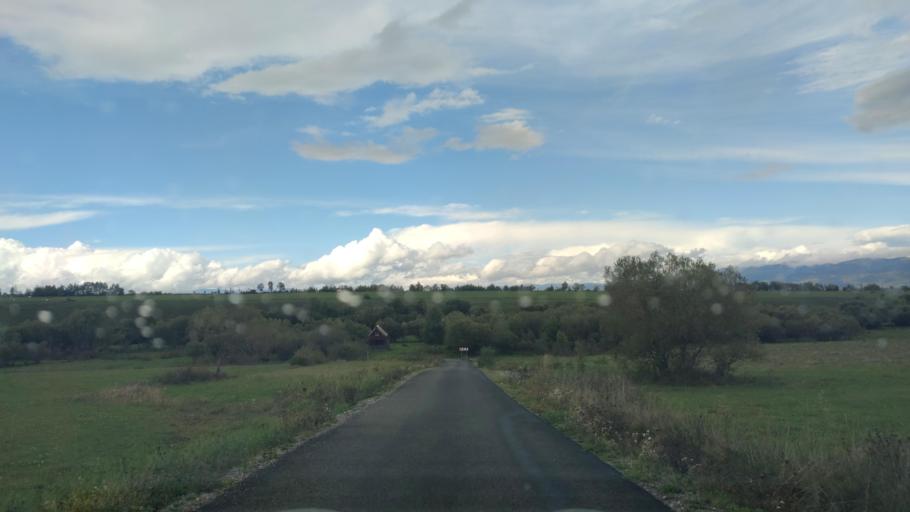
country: RO
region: Harghita
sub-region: Comuna Remetea
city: Remetea
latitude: 46.8126
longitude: 25.3895
